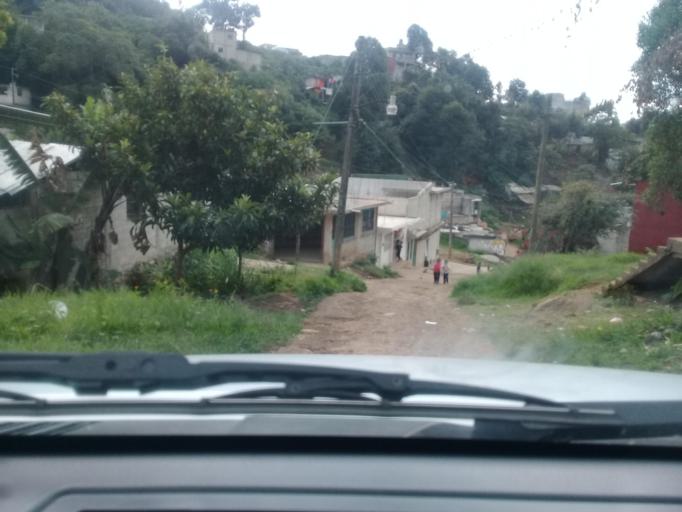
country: MX
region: Veracruz
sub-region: Tlalnelhuayocan
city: Guadalupe Victoria
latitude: 19.5583
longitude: -96.9571
